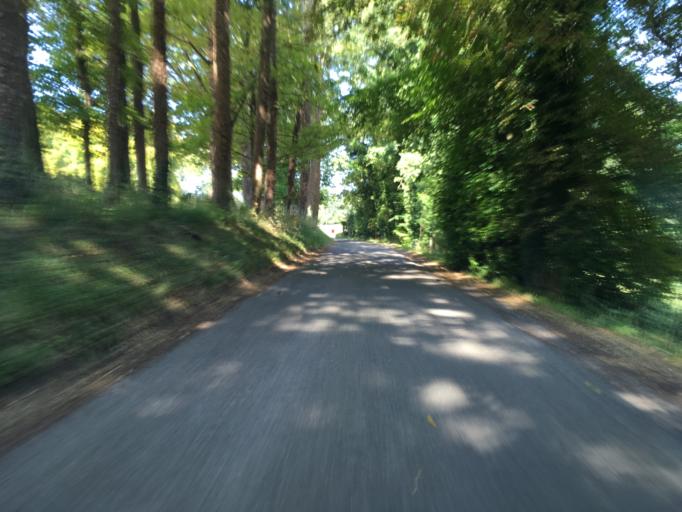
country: GB
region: England
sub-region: Hampshire
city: Highclere
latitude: 51.2776
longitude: -1.3503
